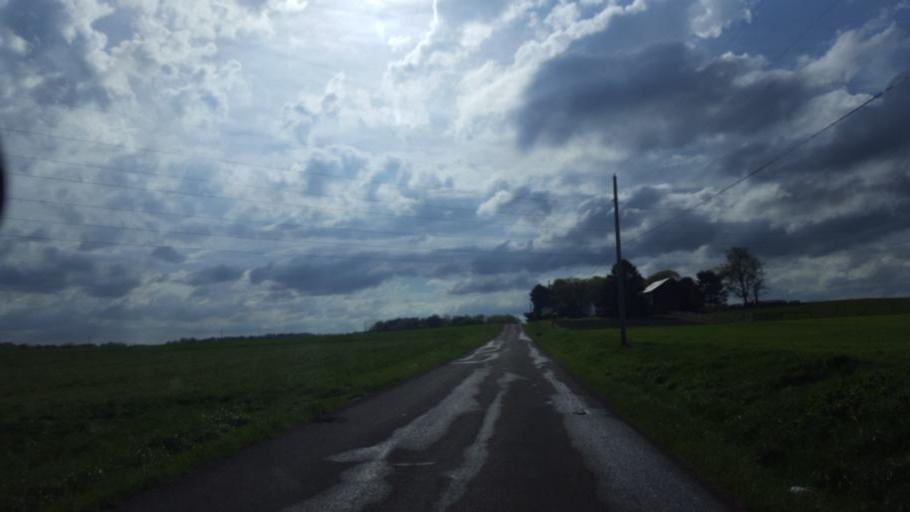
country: US
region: Ohio
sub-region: Knox County
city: Gambier
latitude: 40.4922
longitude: -82.3787
